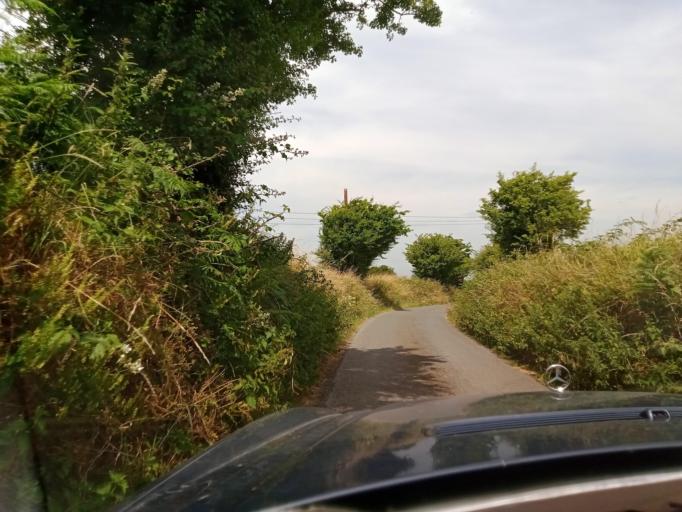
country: IE
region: Leinster
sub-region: Kilkenny
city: Mooncoin
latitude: 52.2624
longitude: -7.2158
